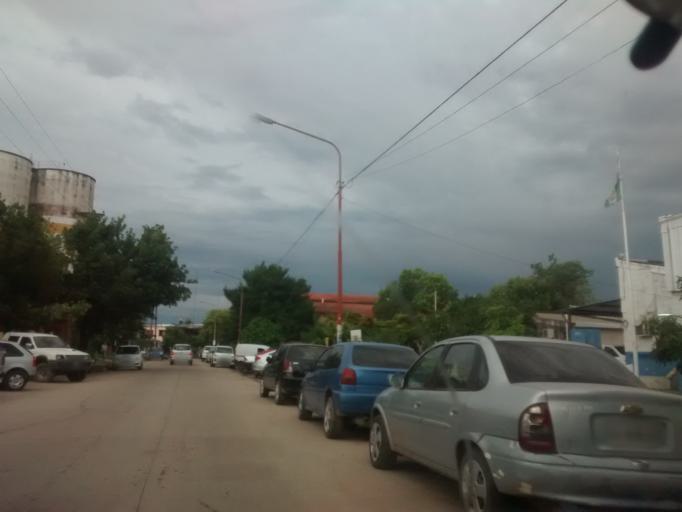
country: AR
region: Chaco
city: Fontana
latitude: -27.4452
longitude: -59.0171
